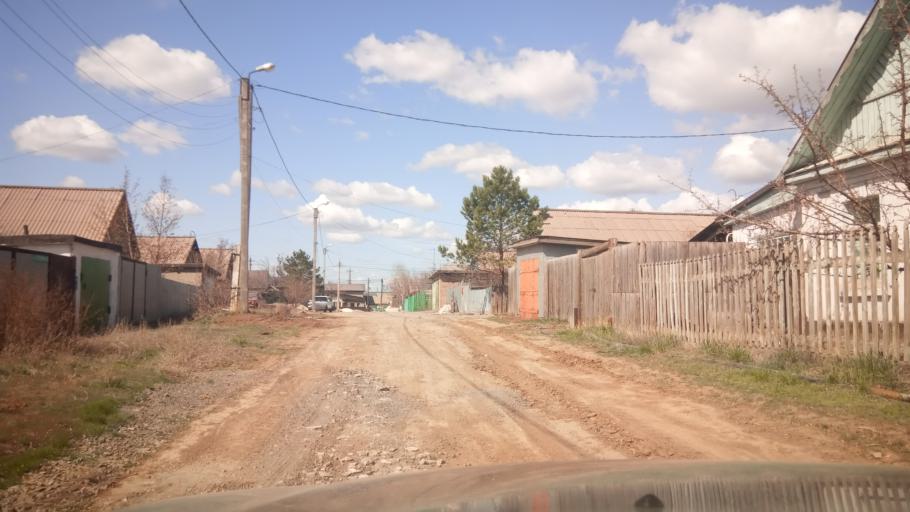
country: RU
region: Orenburg
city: Novotroitsk
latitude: 51.2113
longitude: 58.3164
